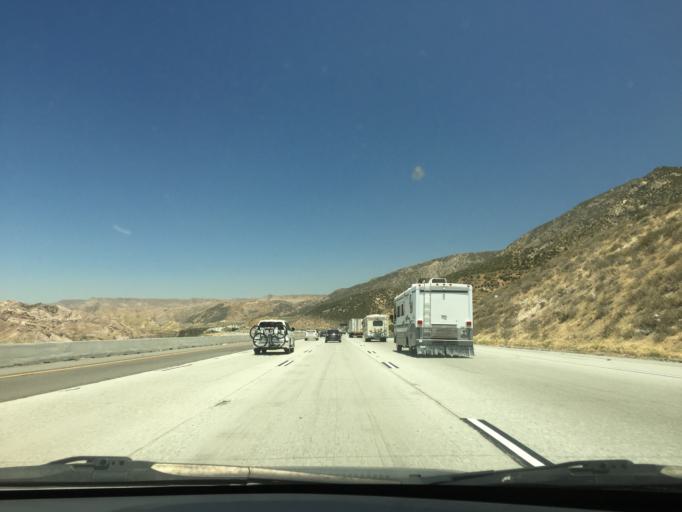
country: US
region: California
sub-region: San Bernardino County
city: Oak Hills
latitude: 34.2687
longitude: -117.4495
